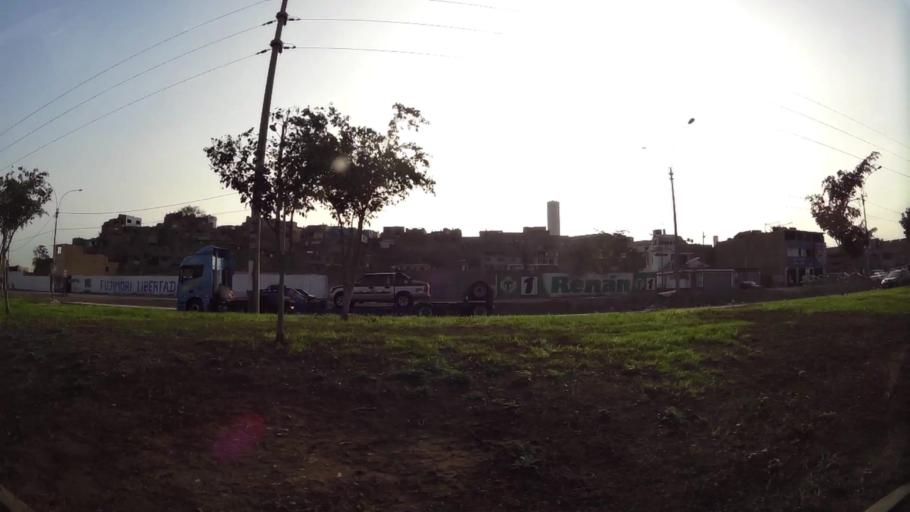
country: PE
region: Lima
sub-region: Lima
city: Independencia
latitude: -11.9673
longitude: -77.0835
